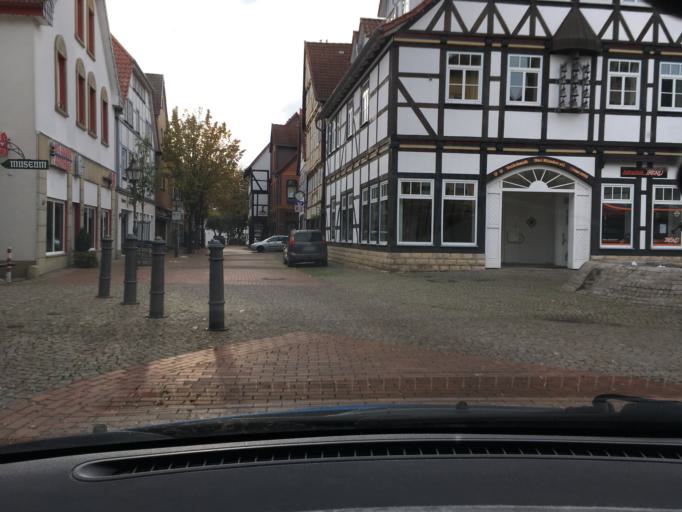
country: DE
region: Lower Saxony
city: Bad Munder am Deister
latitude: 52.1983
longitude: 9.4631
